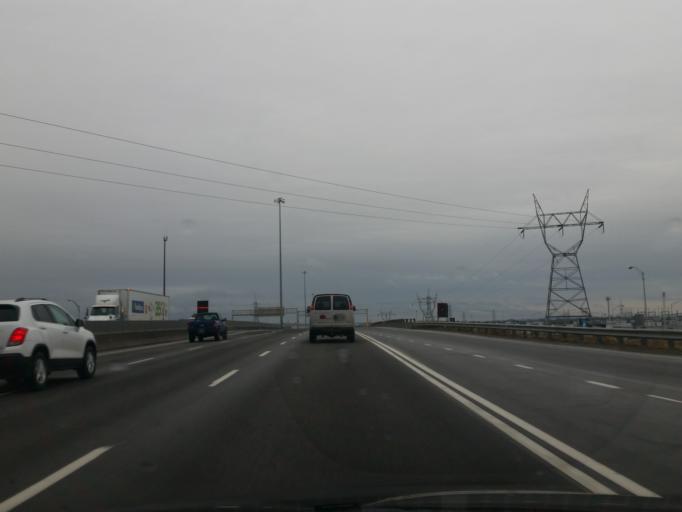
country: CA
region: Quebec
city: Quebec
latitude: 46.8304
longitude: -71.2797
